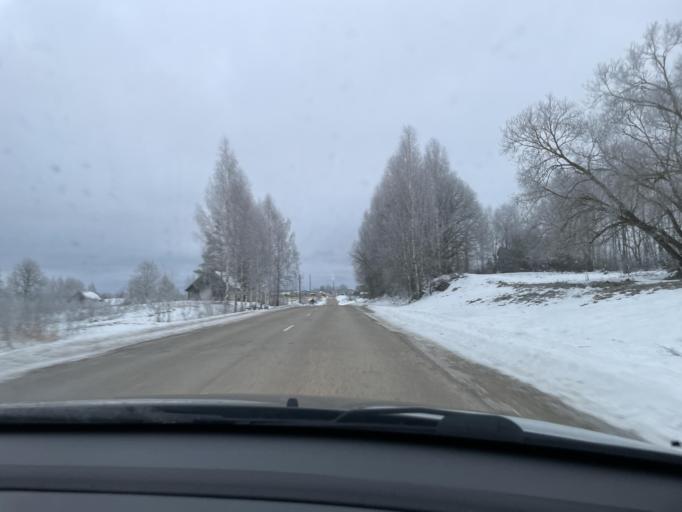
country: LV
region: Ludzas Rajons
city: Ludza
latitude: 56.4367
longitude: 27.5362
